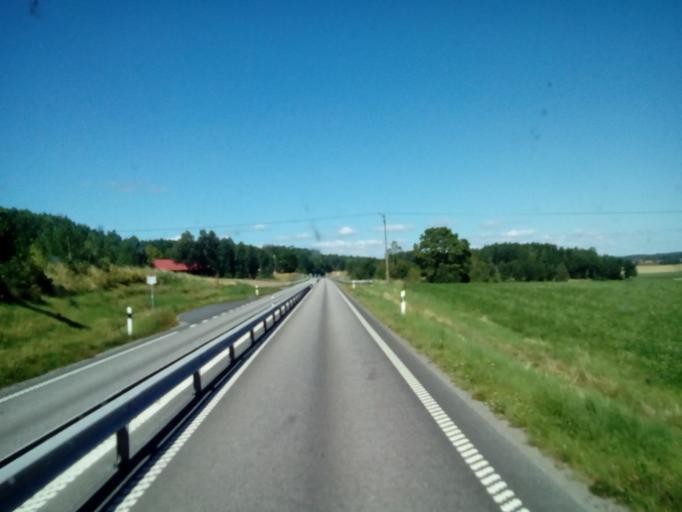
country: SE
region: OEstergoetland
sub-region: Kinda Kommun
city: Rimforsa
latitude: 58.1141
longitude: 15.6709
